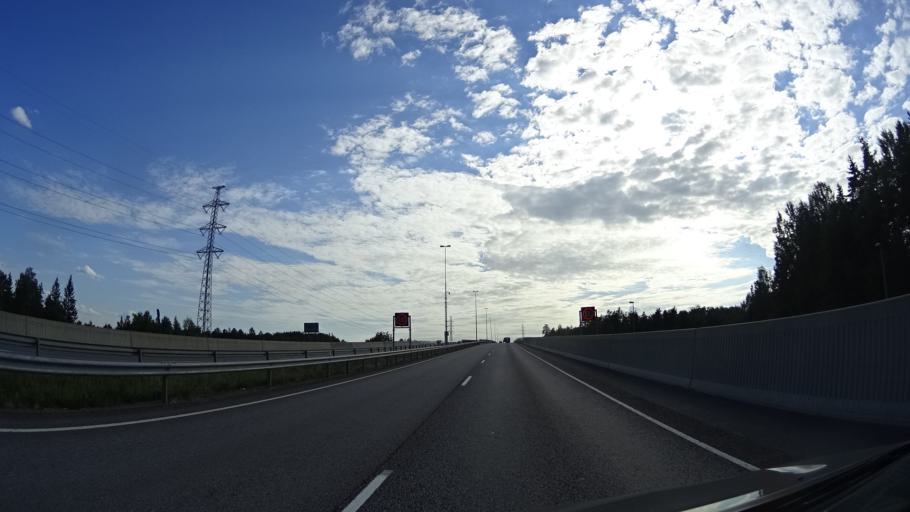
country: FI
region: South Karelia
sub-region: Lappeenranta
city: Lappeenranta
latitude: 61.0720
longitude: 28.3106
